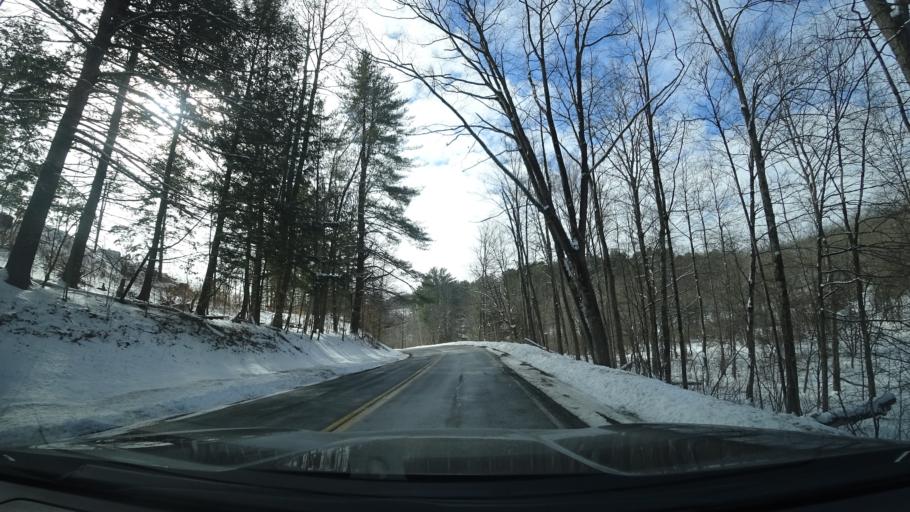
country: US
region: New York
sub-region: Washington County
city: Fort Edward
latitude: 43.2493
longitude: -73.4155
